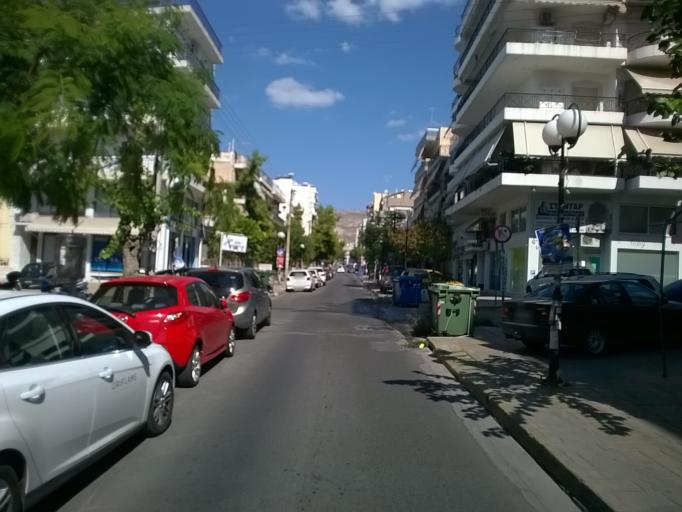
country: GR
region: Attica
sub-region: Nomos Piraios
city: Keratsini
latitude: 37.9647
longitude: 23.6259
